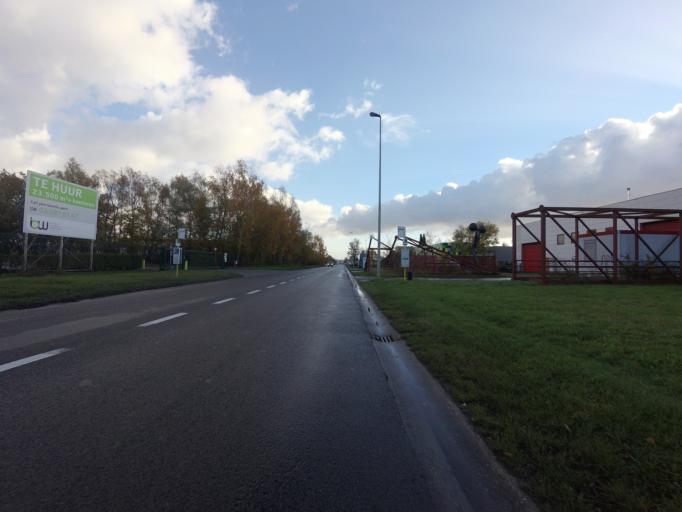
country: BE
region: Flanders
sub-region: Provincie Antwerpen
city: Boom
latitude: 51.0999
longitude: 4.3537
